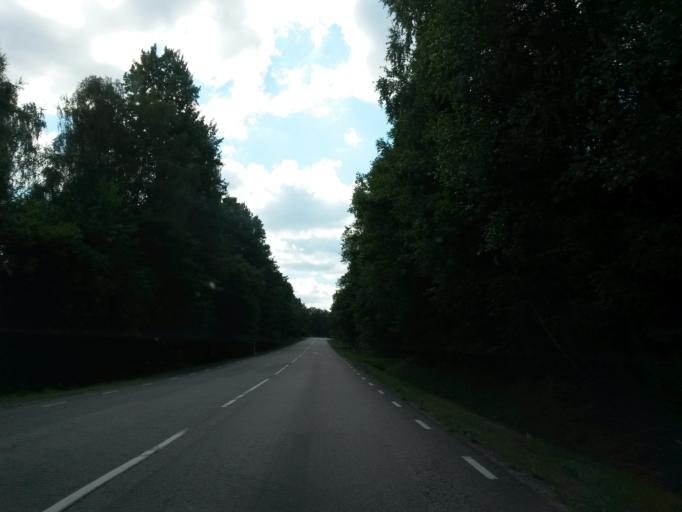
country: SE
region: Vaestra Goetaland
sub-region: Lerums Kommun
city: Grabo
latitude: 57.8676
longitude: 12.3219
